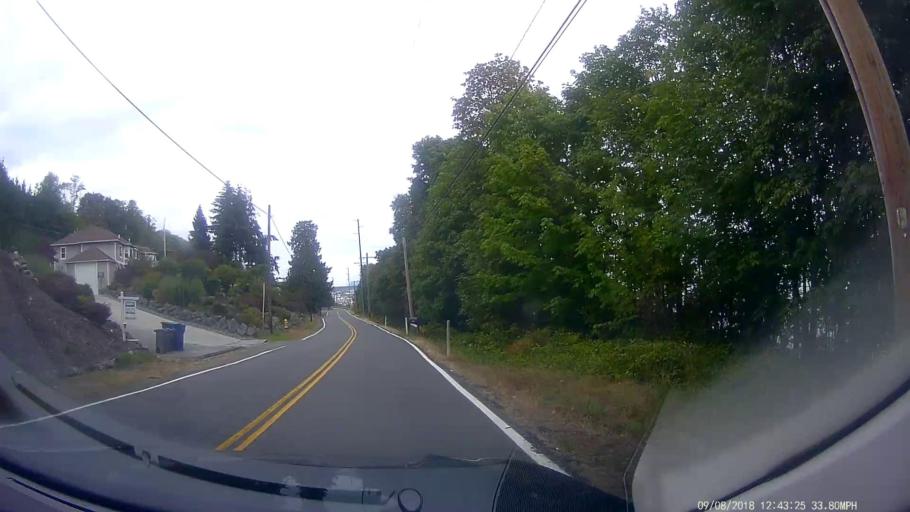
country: US
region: Washington
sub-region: Skagit County
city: Anacortes
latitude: 48.4894
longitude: -122.5993
